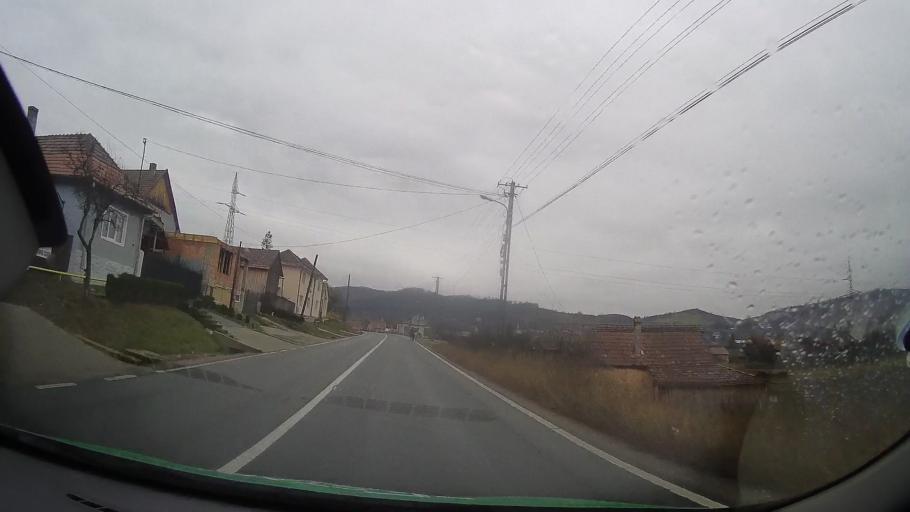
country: RO
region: Bistrita-Nasaud
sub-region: Comuna Teaca
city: Teaca
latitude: 46.9142
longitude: 24.4975
